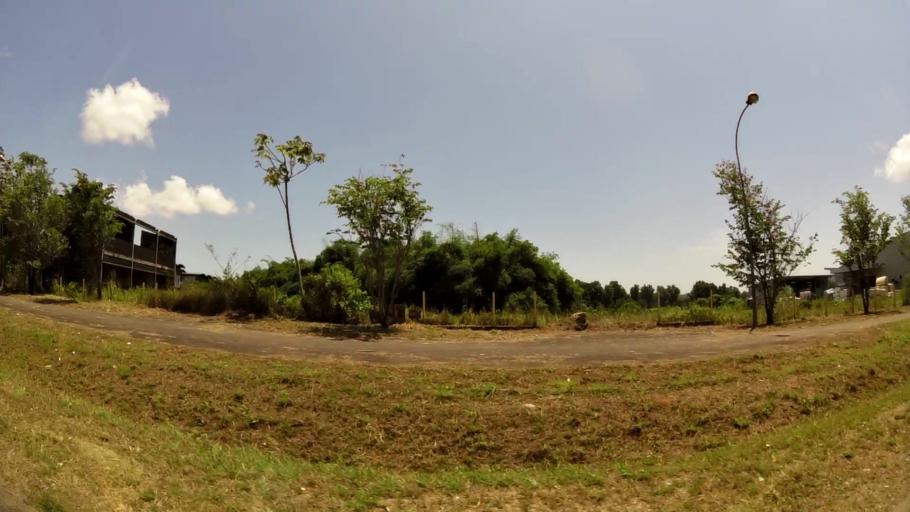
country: GF
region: Guyane
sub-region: Guyane
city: Cayenne
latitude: 4.8978
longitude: -52.3358
